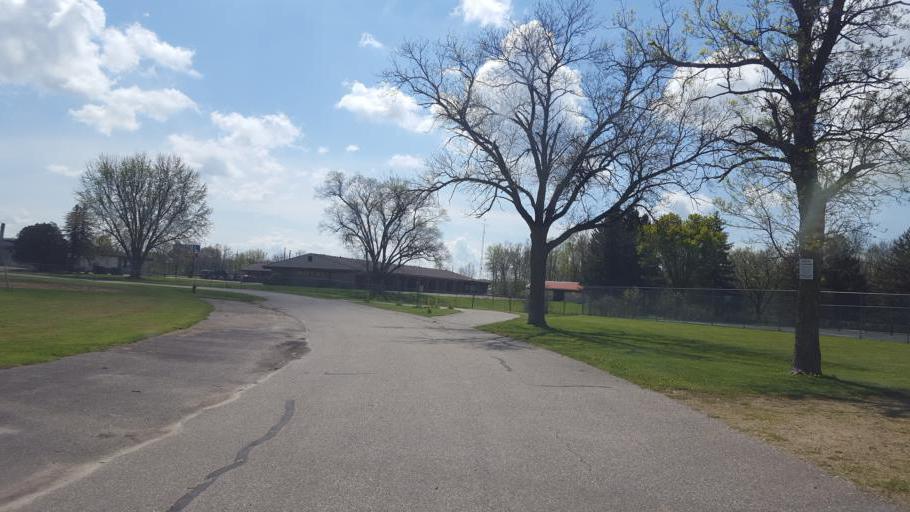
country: US
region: Wisconsin
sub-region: Juneau County
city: Elroy
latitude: 43.7279
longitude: -90.2687
